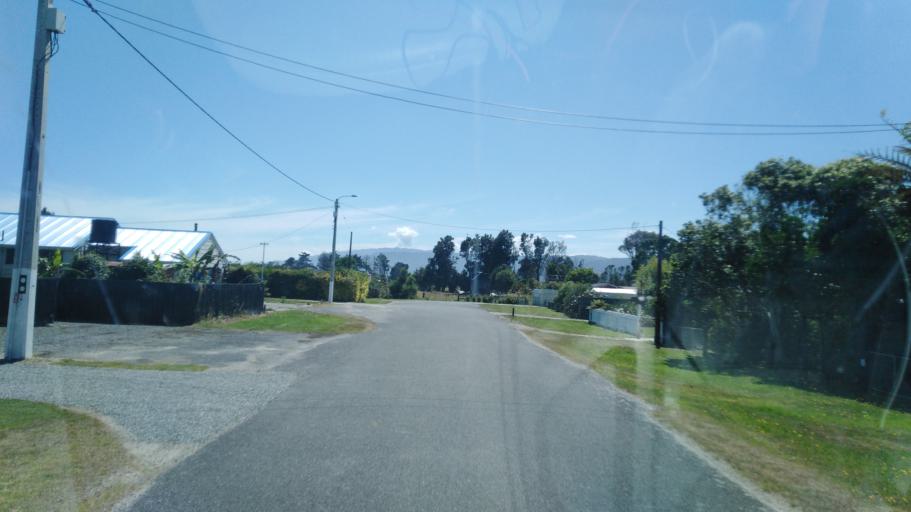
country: NZ
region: West Coast
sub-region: Buller District
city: Westport
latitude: -41.2502
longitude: 172.1092
